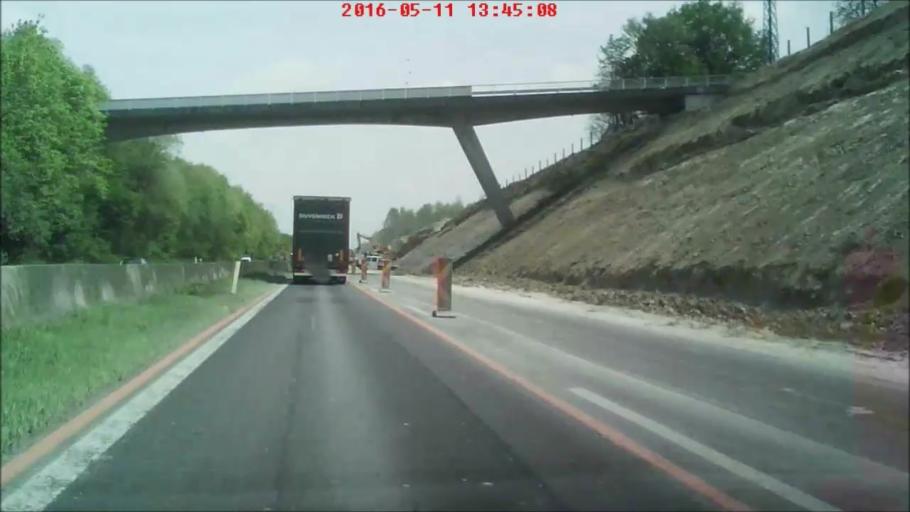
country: AT
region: Upper Austria
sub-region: Politischer Bezirk Vocklabruck
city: Wolfsegg am Hausruck
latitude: 48.2203
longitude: 13.6167
